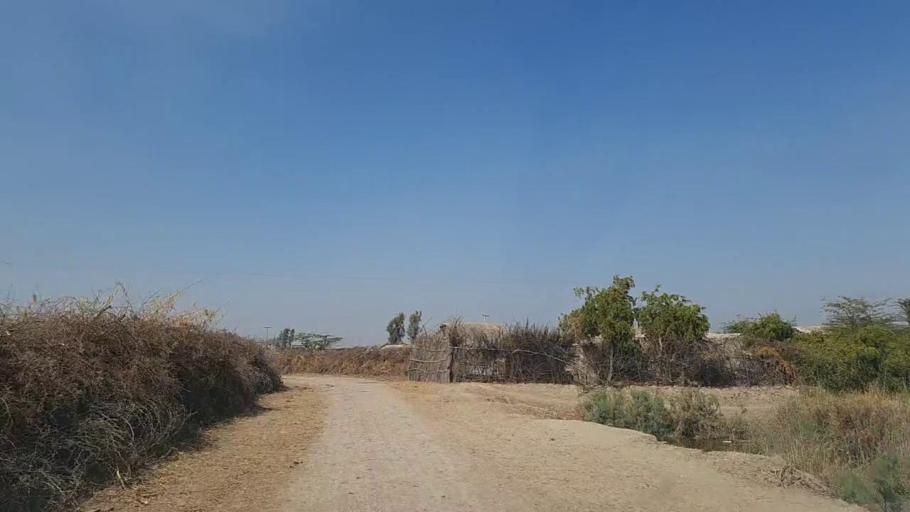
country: PK
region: Sindh
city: Pithoro
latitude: 25.4071
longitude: 69.3098
